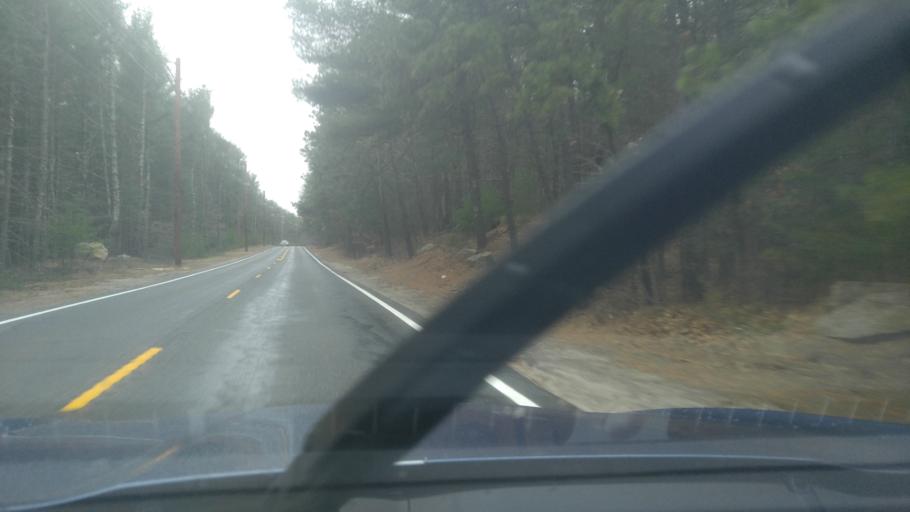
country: US
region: Rhode Island
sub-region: Kent County
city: West Warwick
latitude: 41.6477
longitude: -71.5810
